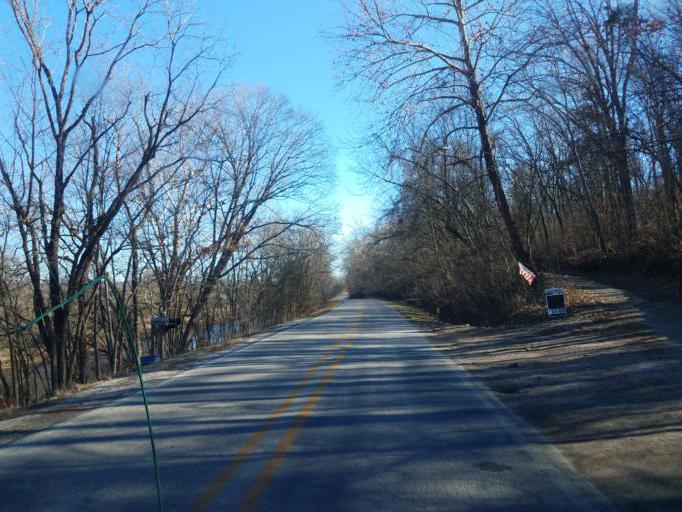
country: US
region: Arkansas
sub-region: Washington County
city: Elkins
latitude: 36.0353
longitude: -93.9500
